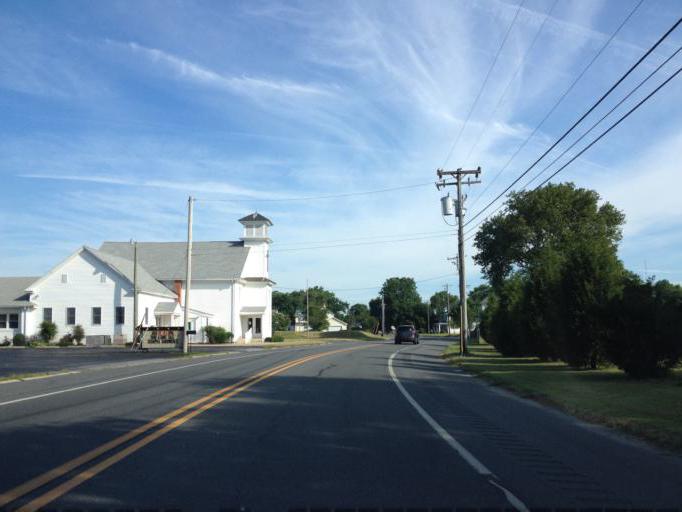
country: US
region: Delaware
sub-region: Sussex County
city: Selbyville
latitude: 38.4929
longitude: -75.1669
